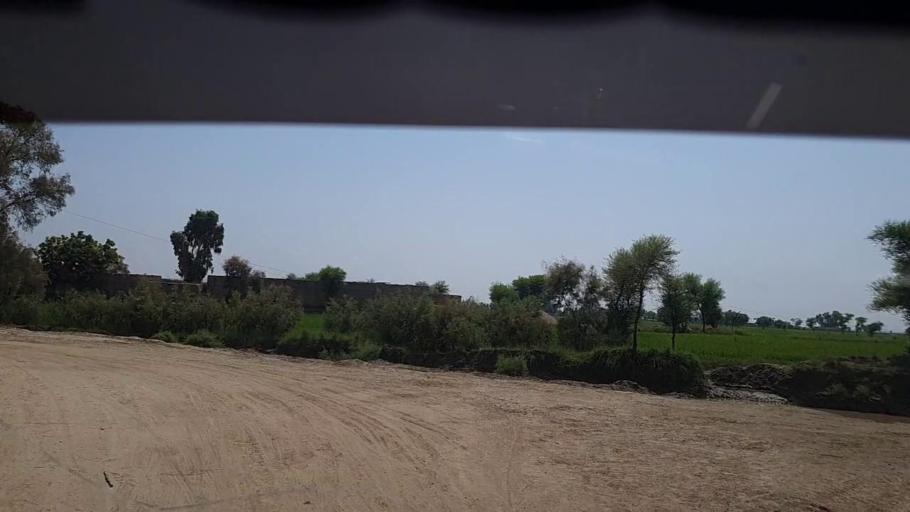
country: PK
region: Sindh
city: Tangwani
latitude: 28.2255
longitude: 68.9026
